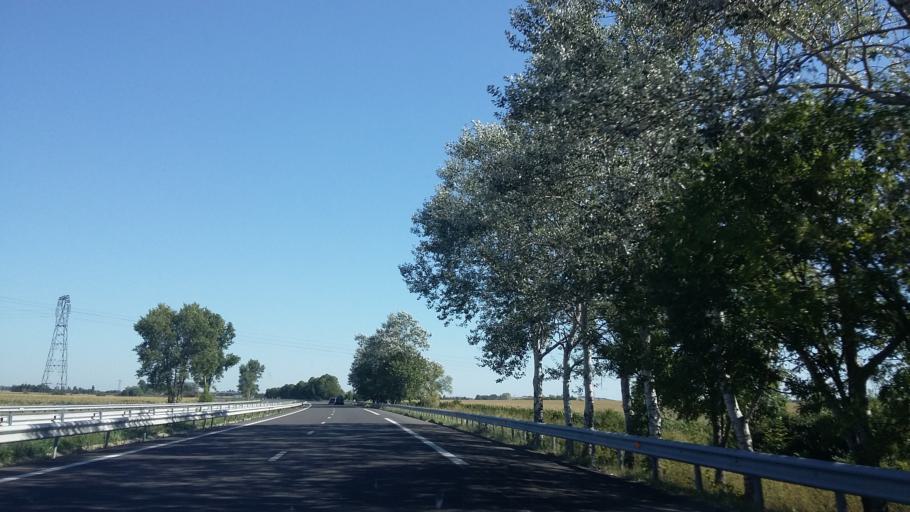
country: FR
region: Auvergne
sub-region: Departement du Puy-de-Dome
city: Pont-du-Chateau
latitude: 45.8072
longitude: 3.2196
